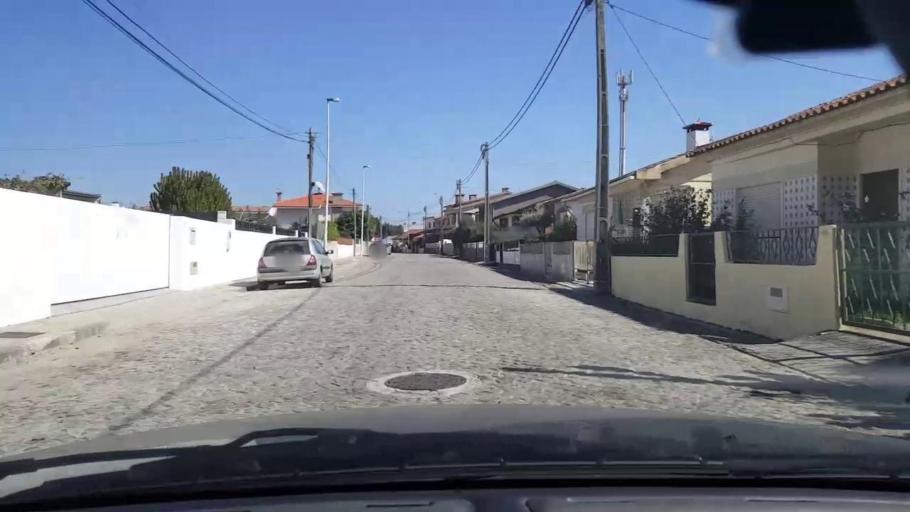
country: PT
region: Porto
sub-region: Matosinhos
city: Lavra
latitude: 41.2979
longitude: -8.7276
